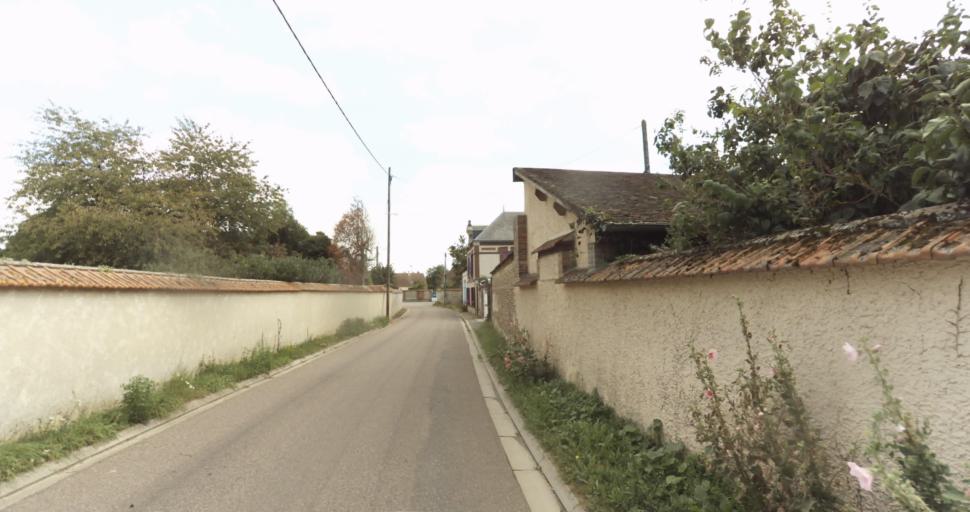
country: FR
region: Haute-Normandie
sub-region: Departement de l'Eure
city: La Madeleine-de-Nonancourt
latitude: 48.8298
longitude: 1.1756
